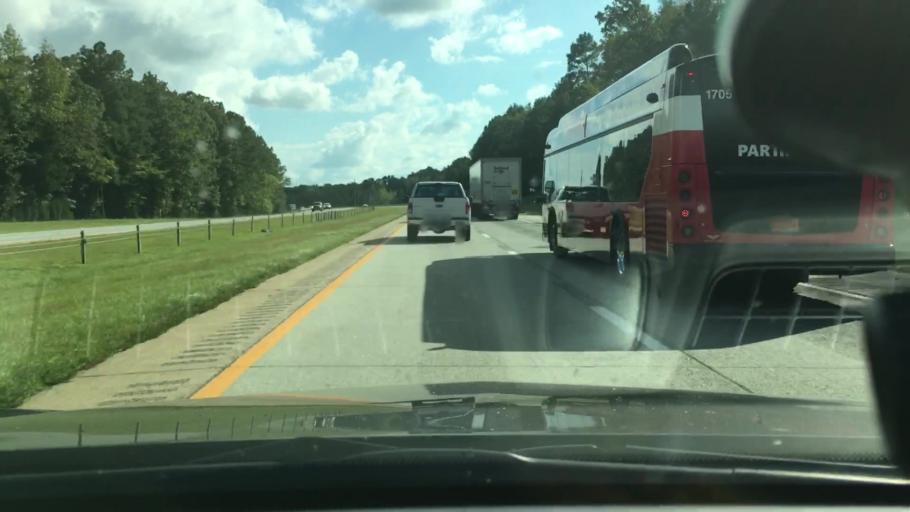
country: US
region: North Carolina
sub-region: Orange County
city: Chapel Hill
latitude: 35.9914
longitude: -79.0756
